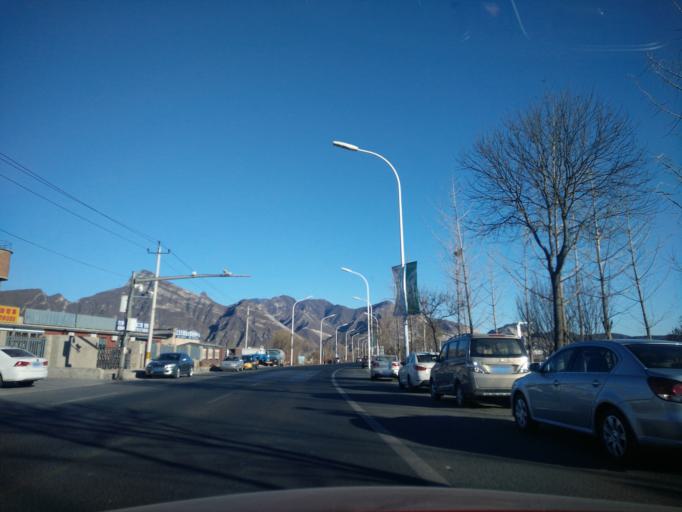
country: CN
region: Beijing
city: Junzhuang
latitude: 39.9849
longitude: 116.0810
